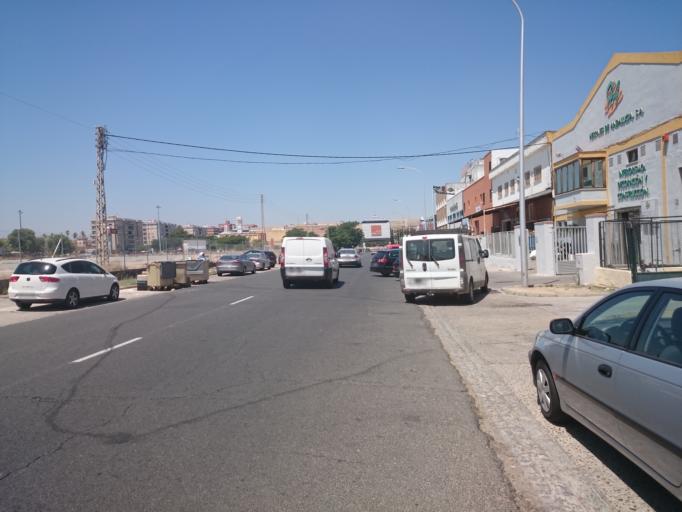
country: ES
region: Andalusia
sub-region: Provincia de Sevilla
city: Sevilla
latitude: 37.3886
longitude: -5.9556
